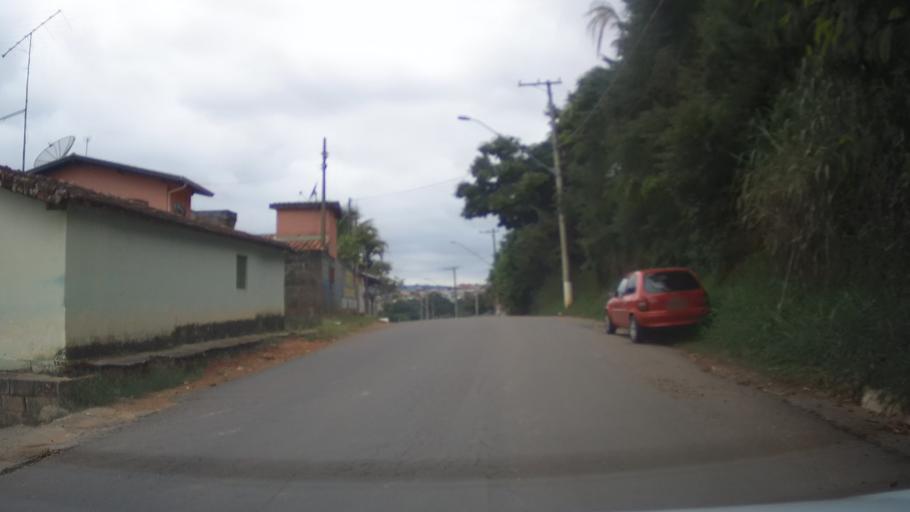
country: BR
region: Sao Paulo
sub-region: Louveira
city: Louveira
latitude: -23.0964
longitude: -46.9883
